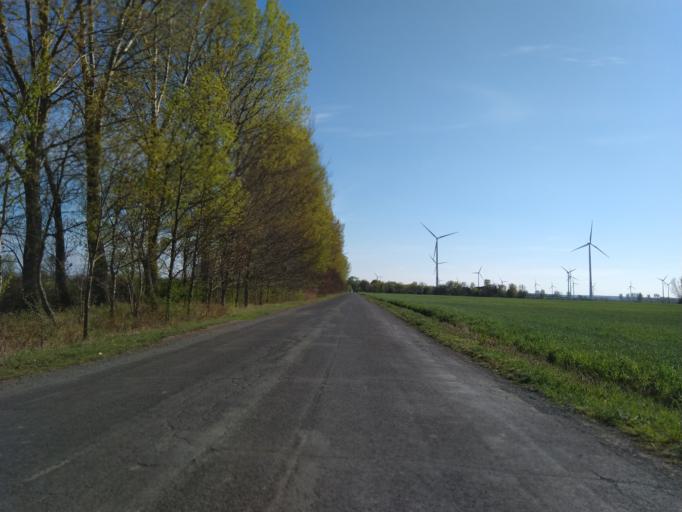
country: DE
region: Brandenburg
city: Neutrebbin
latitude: 52.7214
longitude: 14.2128
